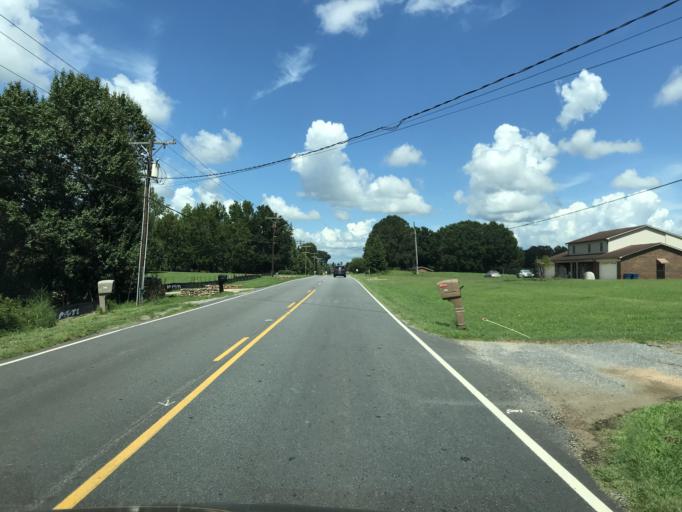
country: US
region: North Carolina
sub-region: Catawba County
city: Lake Norman of Catawba
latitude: 35.5664
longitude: -81.0517
